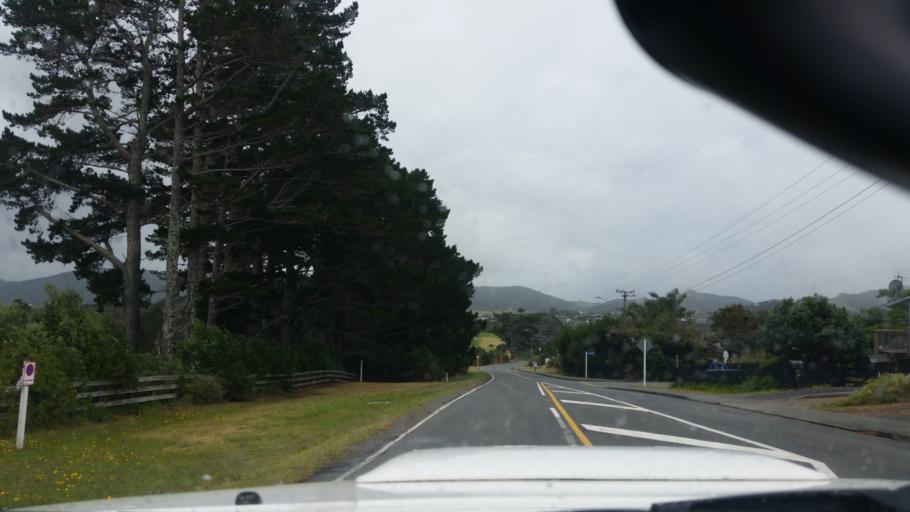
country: NZ
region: Auckland
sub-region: Auckland
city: Wellsford
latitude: -36.0985
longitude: 174.5874
